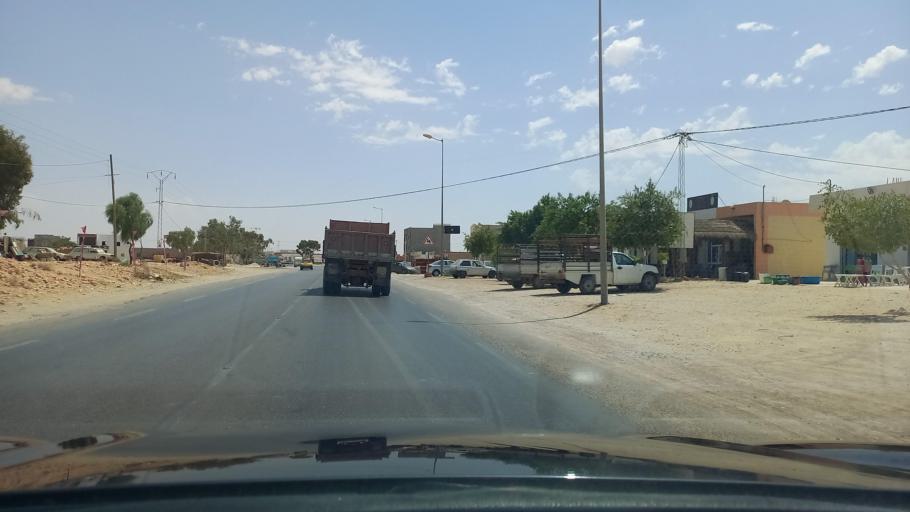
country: TN
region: Madanin
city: Medenine
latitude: 33.3706
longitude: 10.4485
